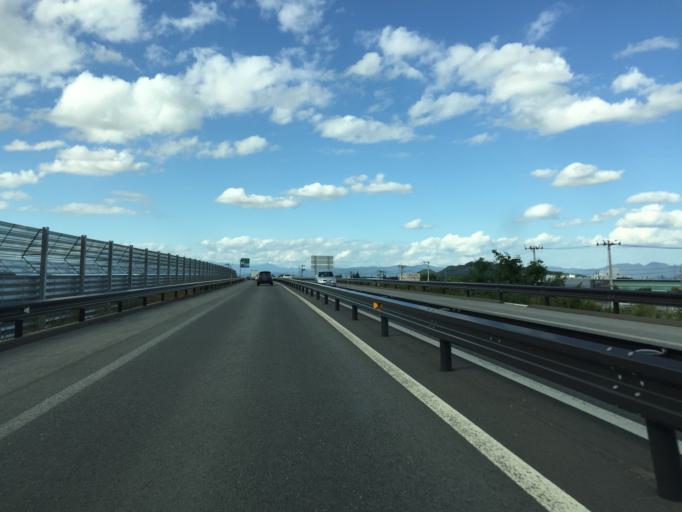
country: JP
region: Yamagata
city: Yonezawa
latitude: 37.9078
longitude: 140.1422
